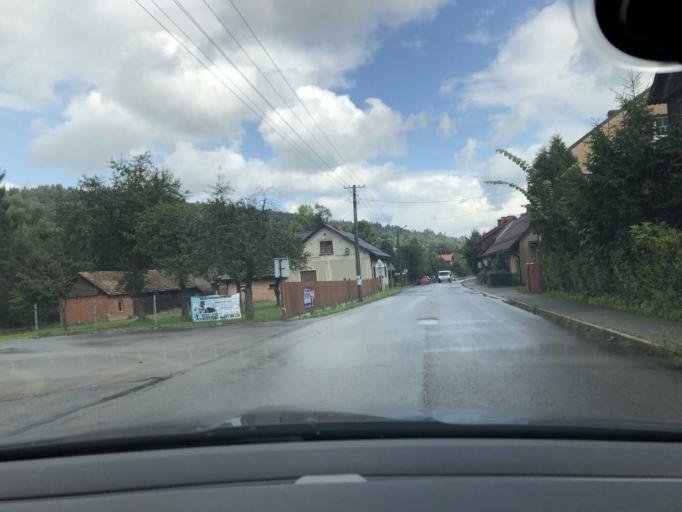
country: PL
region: Lesser Poland Voivodeship
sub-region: Powiat suski
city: Lachowice
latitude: 49.7145
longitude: 19.4724
